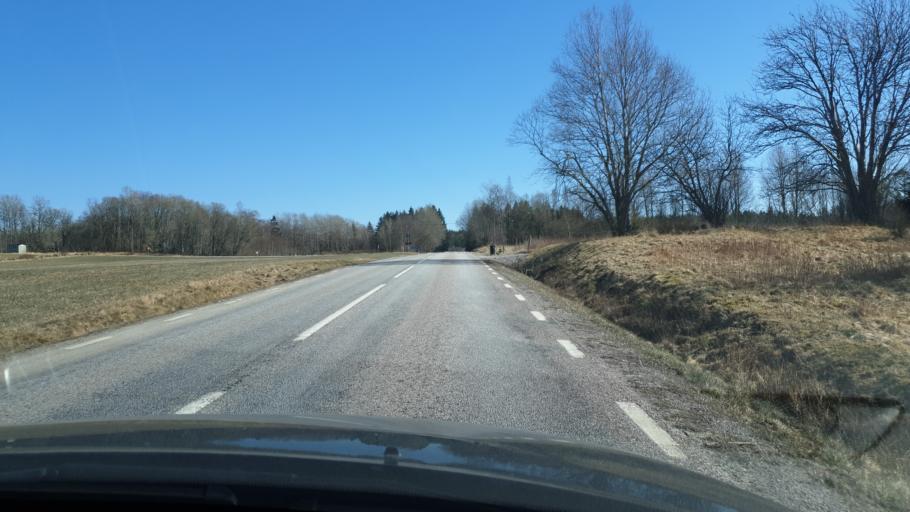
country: SE
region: Vaestra Goetaland
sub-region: Tanums Kommun
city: Tanumshede
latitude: 58.7416
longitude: 11.4743
